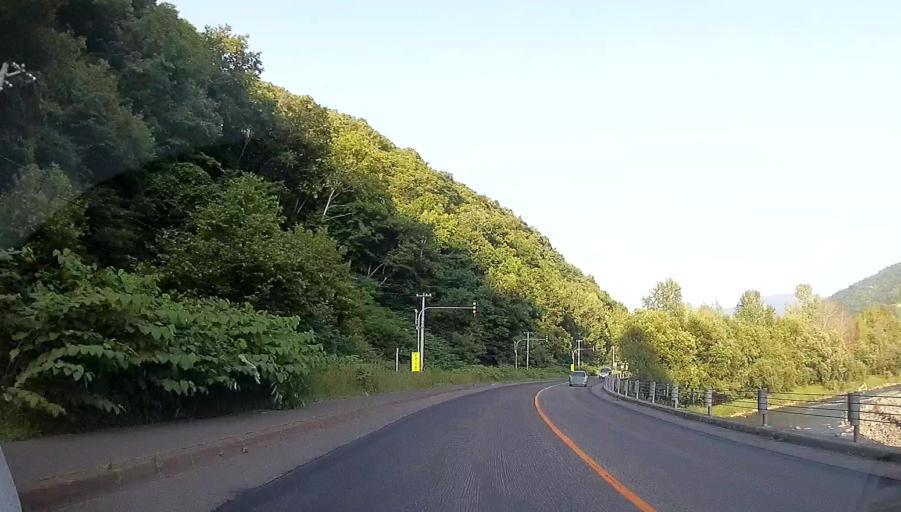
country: JP
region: Hokkaido
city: Shimo-furano
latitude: 42.8958
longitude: 142.4988
